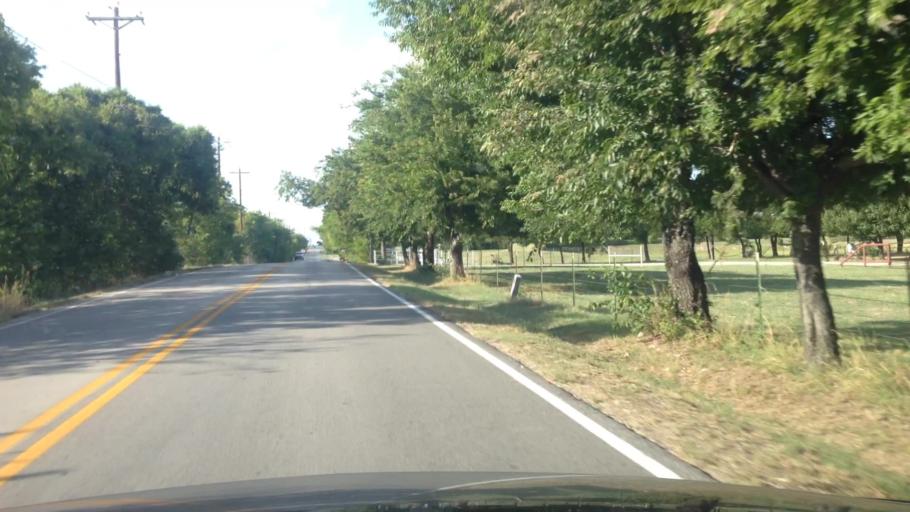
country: US
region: Texas
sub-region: Tarrant County
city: Haslet
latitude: 32.9320
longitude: -97.3920
